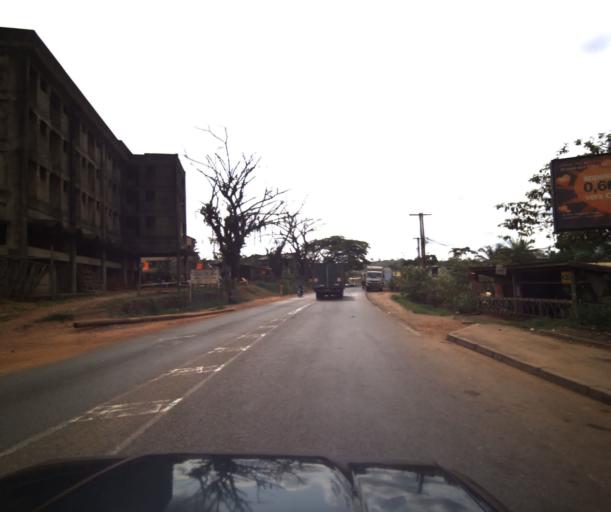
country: CM
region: Littoral
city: Edea
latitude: 3.7908
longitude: 10.1392
